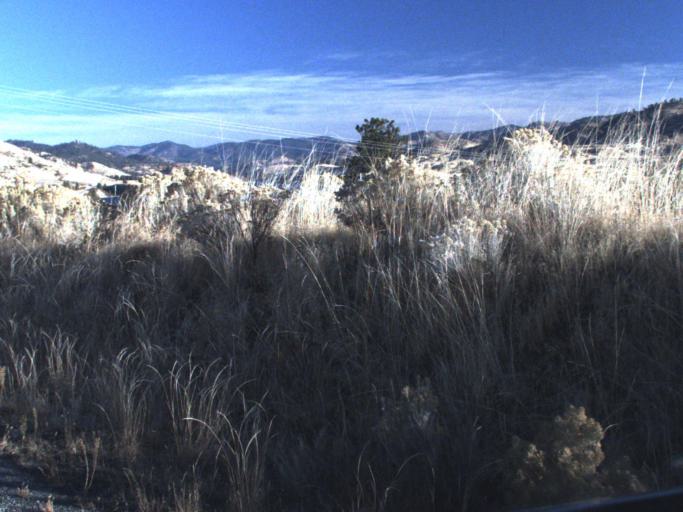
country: US
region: Washington
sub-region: Okanogan County
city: Coulee Dam
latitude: 47.9614
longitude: -118.7002
